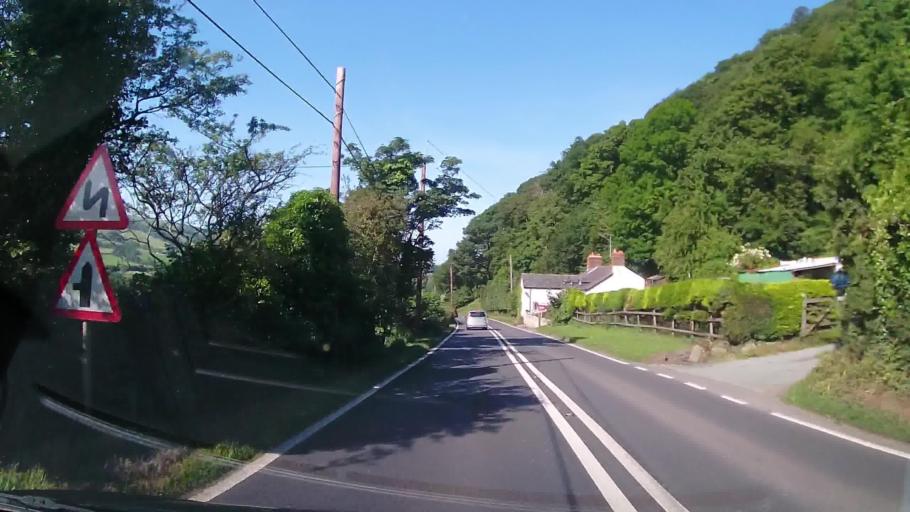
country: GB
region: England
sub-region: Shropshire
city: Pant
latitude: 52.6986
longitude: -3.0549
